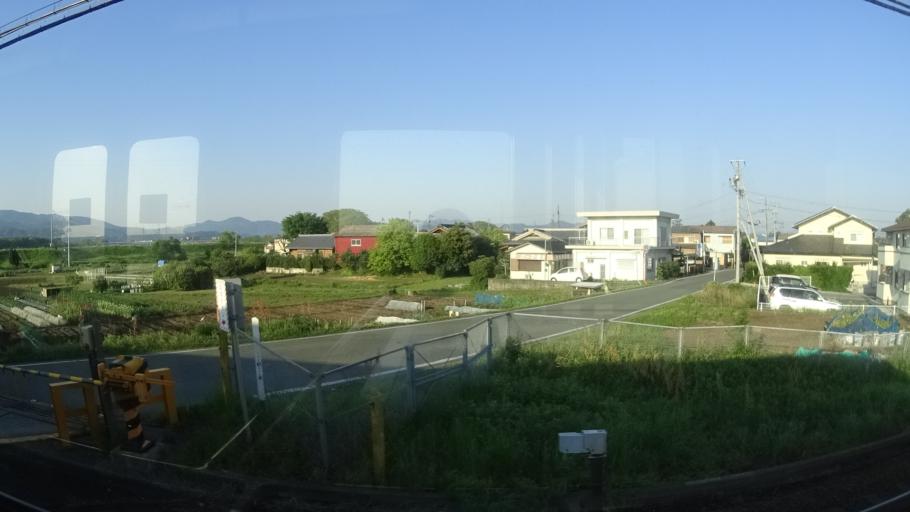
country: JP
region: Mie
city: Ise
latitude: 34.5116
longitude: 136.6864
